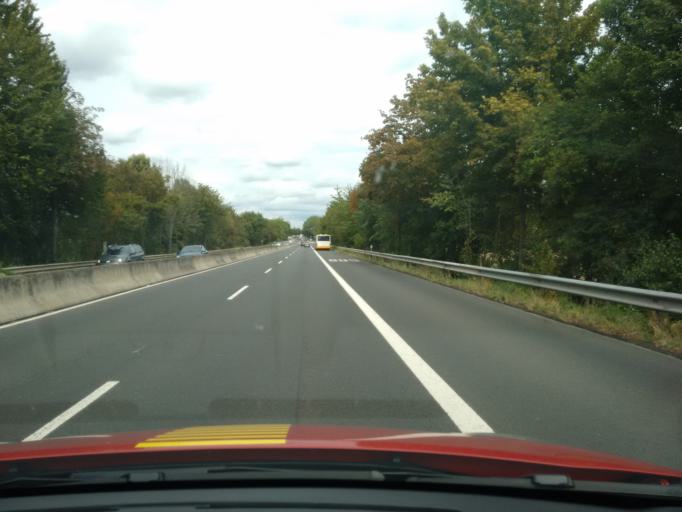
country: DE
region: Rheinland-Pfalz
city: Mainz
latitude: 49.9809
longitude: 8.2593
